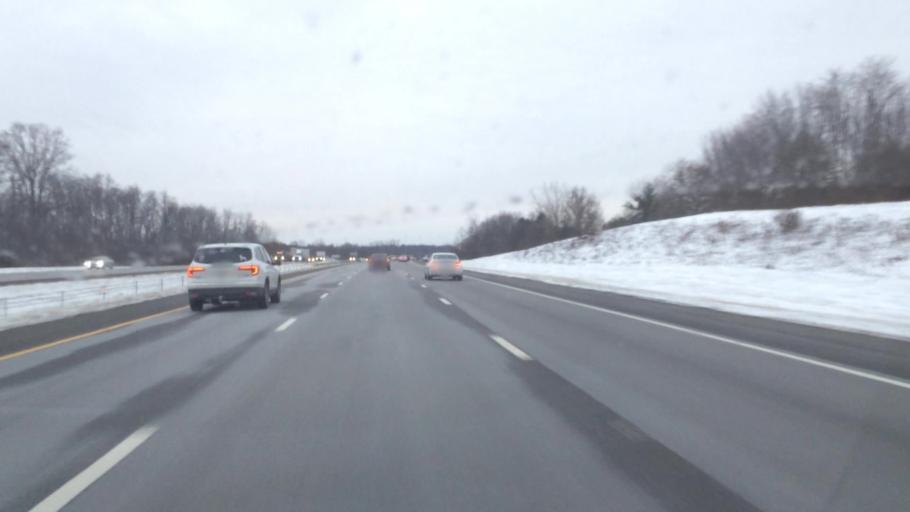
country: US
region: Ohio
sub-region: Medina County
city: Medina
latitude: 41.1713
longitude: -81.7864
